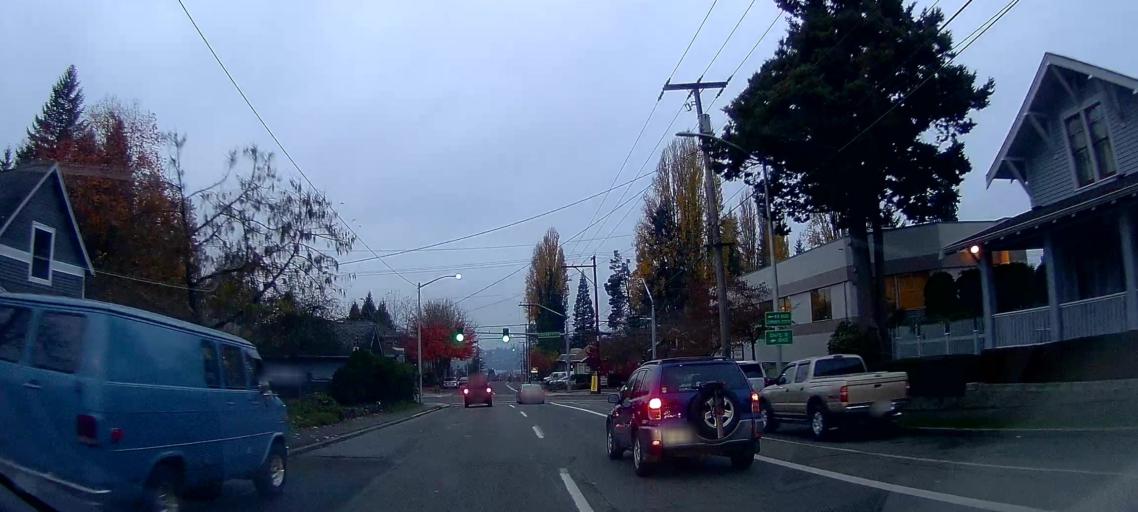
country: US
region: Washington
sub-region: Thurston County
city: Olympia
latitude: 47.0469
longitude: -122.8812
